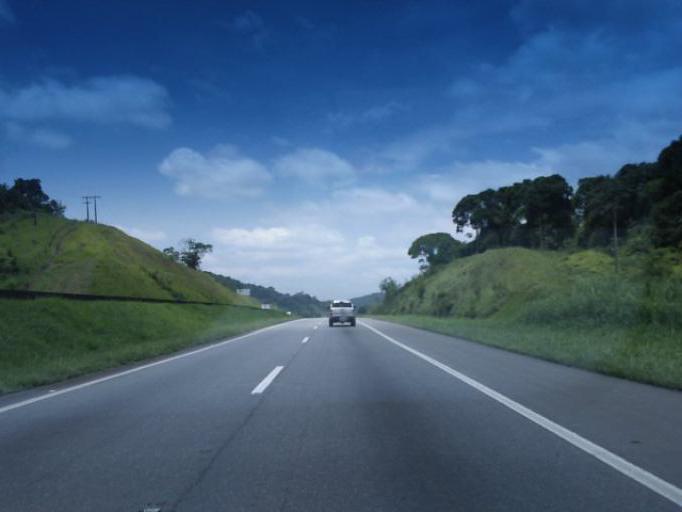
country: BR
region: Sao Paulo
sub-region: Miracatu
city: Miracatu
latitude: -24.1736
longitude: -47.3432
